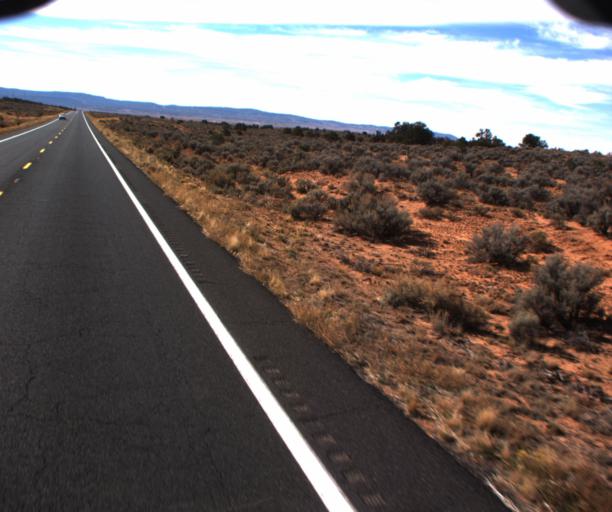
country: US
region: Arizona
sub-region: Coconino County
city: Kaibito
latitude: 36.5386
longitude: -110.7011
